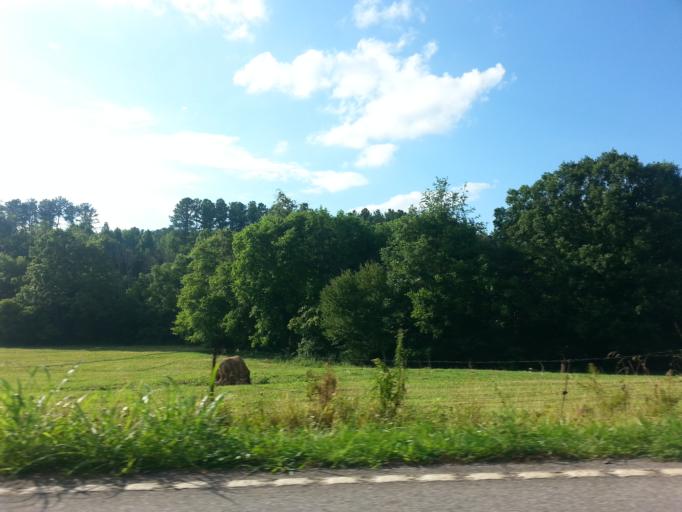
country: US
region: Tennessee
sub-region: Blount County
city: Maryville
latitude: 35.6224
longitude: -84.0283
